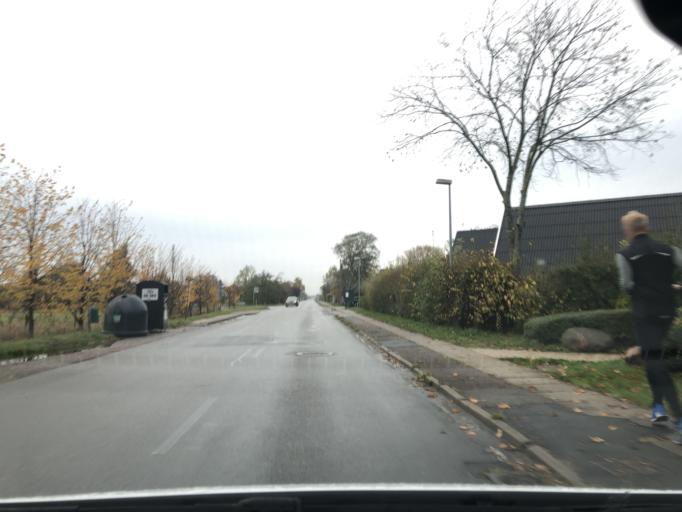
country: DK
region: Capital Region
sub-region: Dragor Kommune
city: Dragor
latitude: 55.5733
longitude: 12.6159
